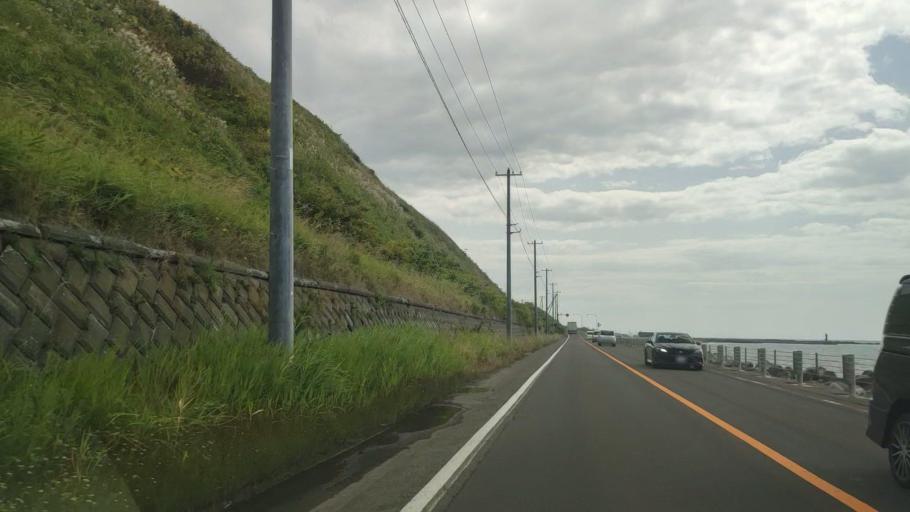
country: JP
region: Hokkaido
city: Rumoi
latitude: 44.5420
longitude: 141.7664
